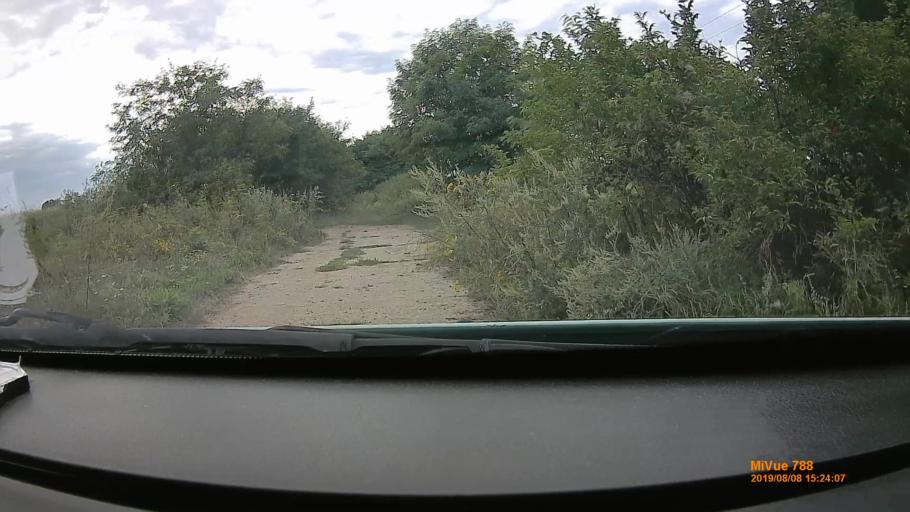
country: HU
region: Szabolcs-Szatmar-Bereg
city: Tunyogmatolcs
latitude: 47.9523
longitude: 22.4346
